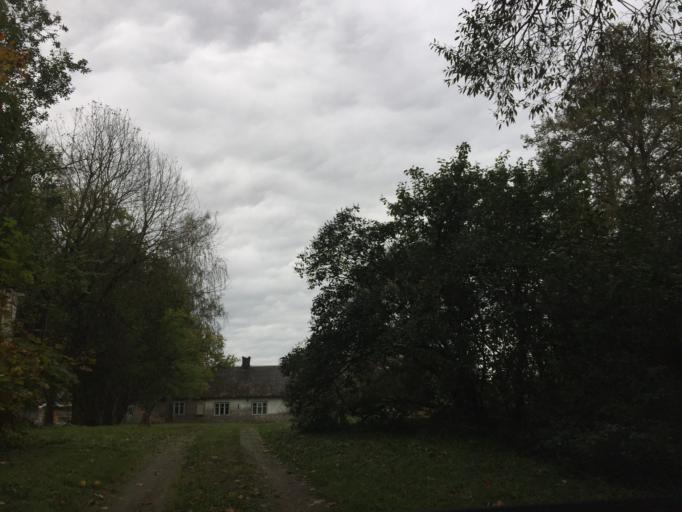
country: LV
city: Tireli
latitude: 56.7802
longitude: 23.6336
